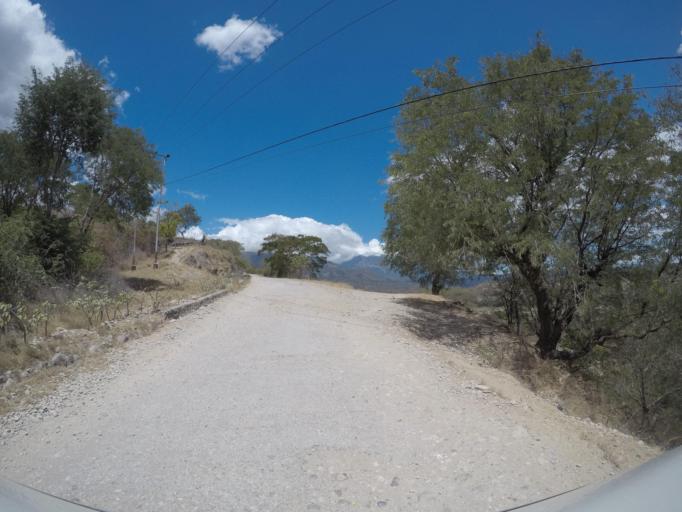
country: TL
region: Baucau
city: Baucau
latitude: -8.4821
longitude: 126.6084
